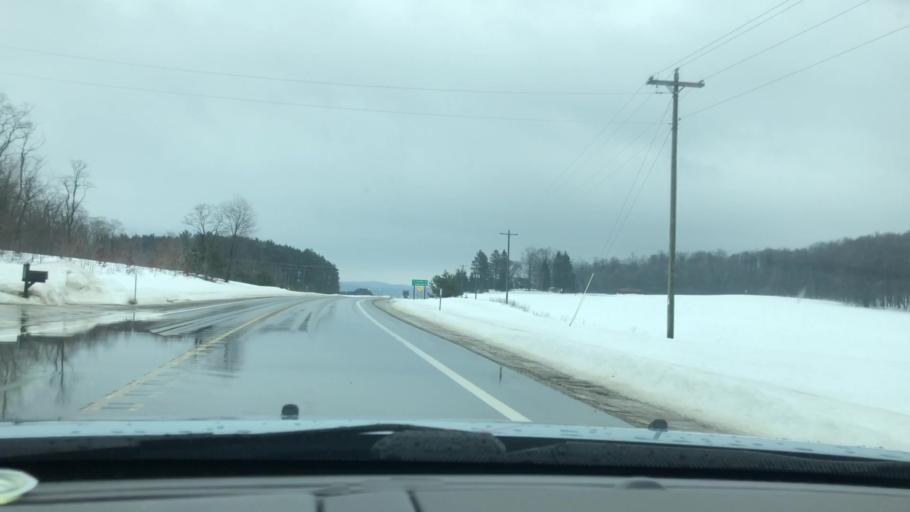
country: US
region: Michigan
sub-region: Charlevoix County
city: Boyne City
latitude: 45.0963
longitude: -84.9831
